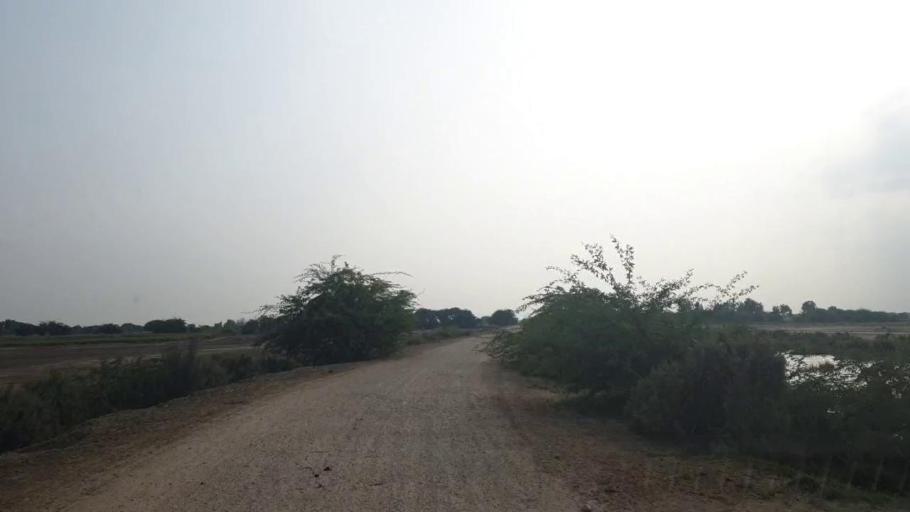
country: PK
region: Sindh
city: Badin
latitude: 24.6287
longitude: 68.6921
